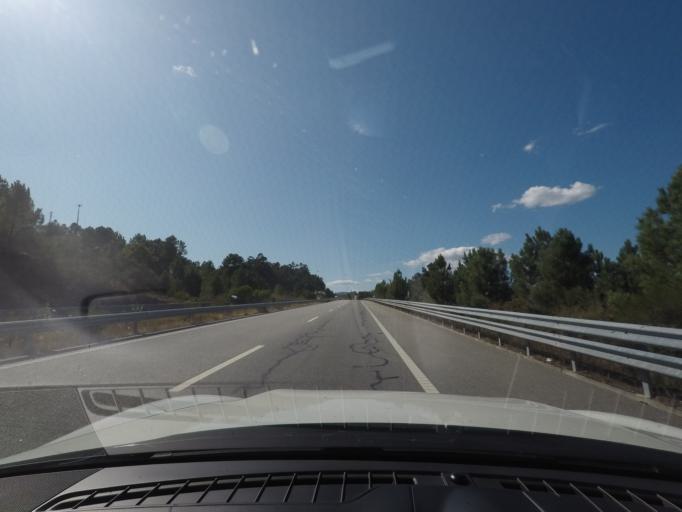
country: PT
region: Vila Real
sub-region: Mondim de Basto
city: Mondim de Basto
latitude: 41.4807
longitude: -7.9127
